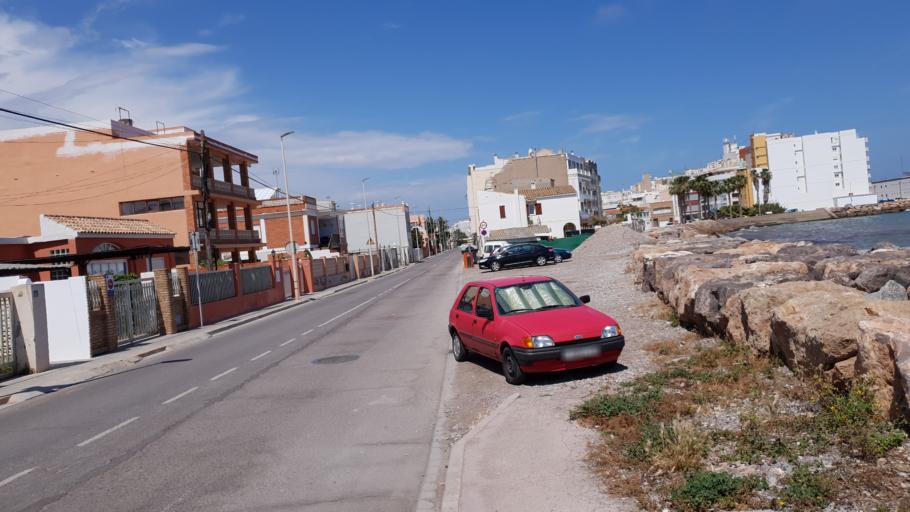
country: ES
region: Valencia
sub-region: Provincia de Castello
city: Burriana
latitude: 39.8621
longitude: -0.0793
